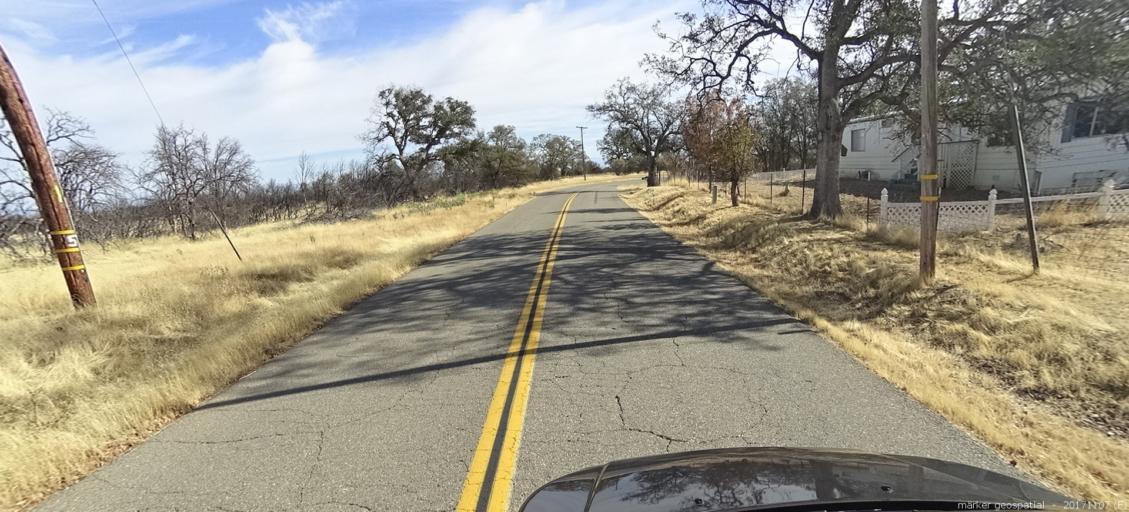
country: US
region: California
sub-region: Shasta County
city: Shasta
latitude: 40.4557
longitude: -122.5344
